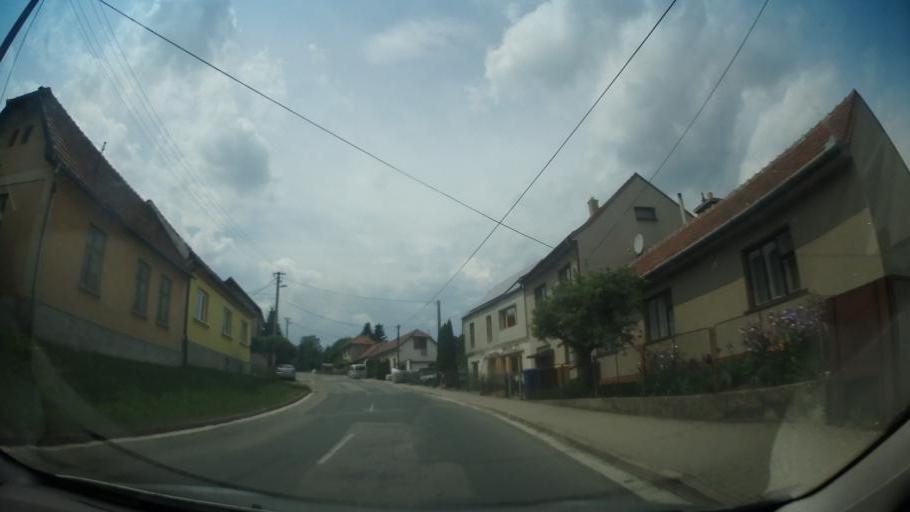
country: CZ
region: South Moravian
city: Lysice
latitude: 49.4507
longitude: 16.5295
